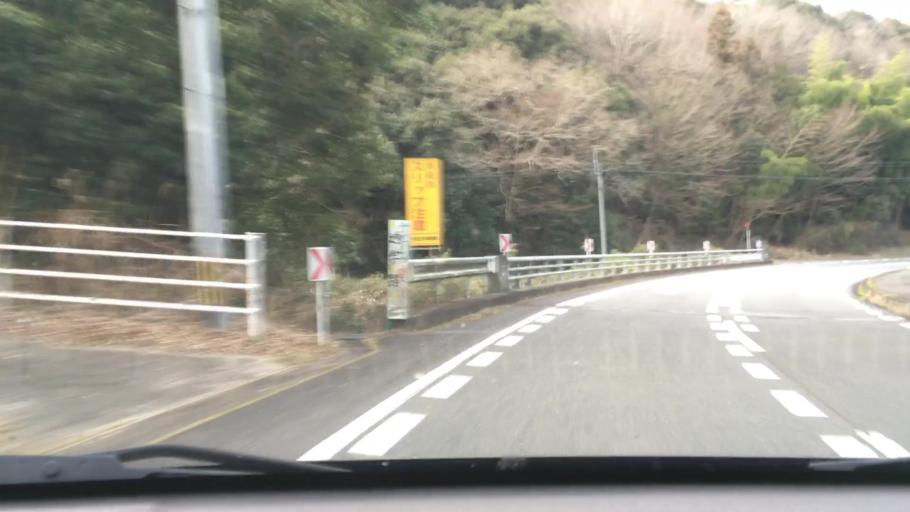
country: JP
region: Oita
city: Hiji
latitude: 33.4237
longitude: 131.4137
